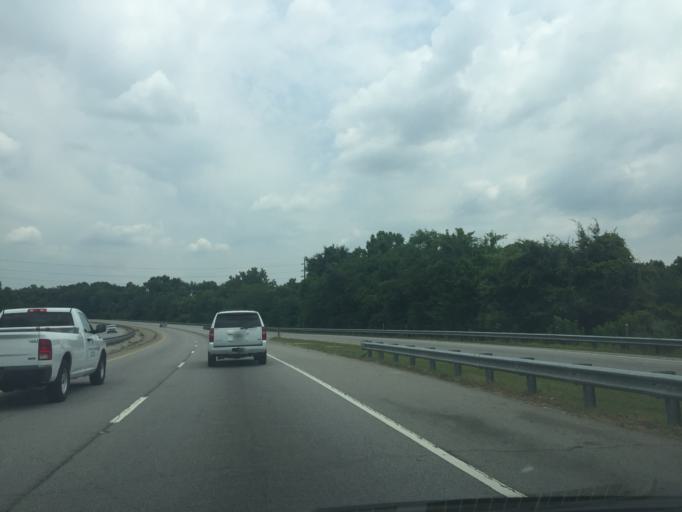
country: US
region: Georgia
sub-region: Chatham County
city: Thunderbolt
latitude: 32.0463
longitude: -81.0688
